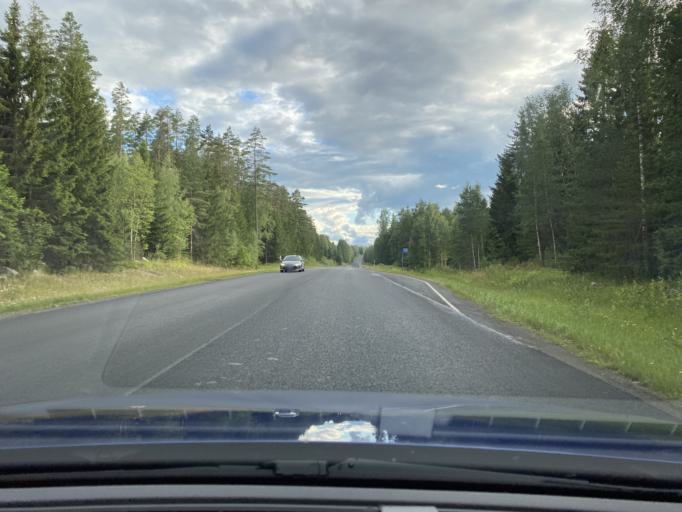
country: FI
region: Haeme
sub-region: Haemeenlinna
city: Haemeenlinna
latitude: 60.9492
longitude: 24.4016
